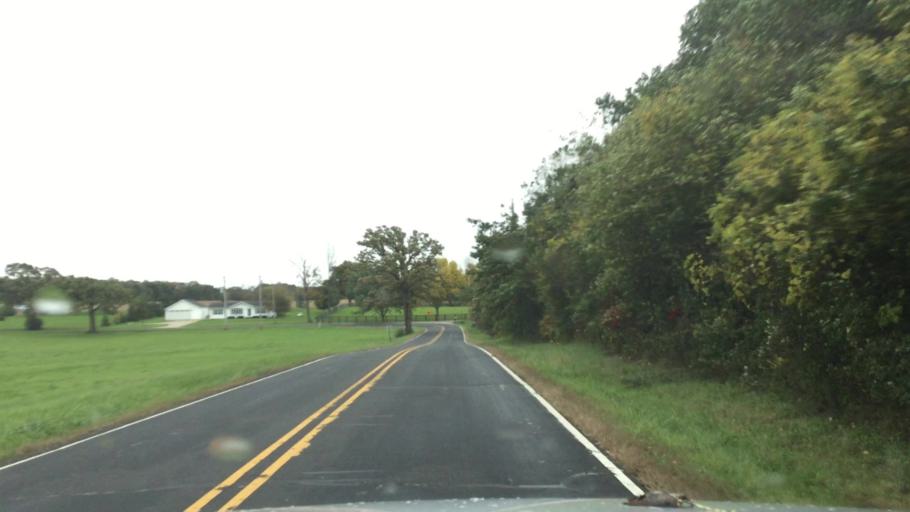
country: US
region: Wisconsin
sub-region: Racine County
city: Waterford
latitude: 42.7586
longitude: -88.1607
